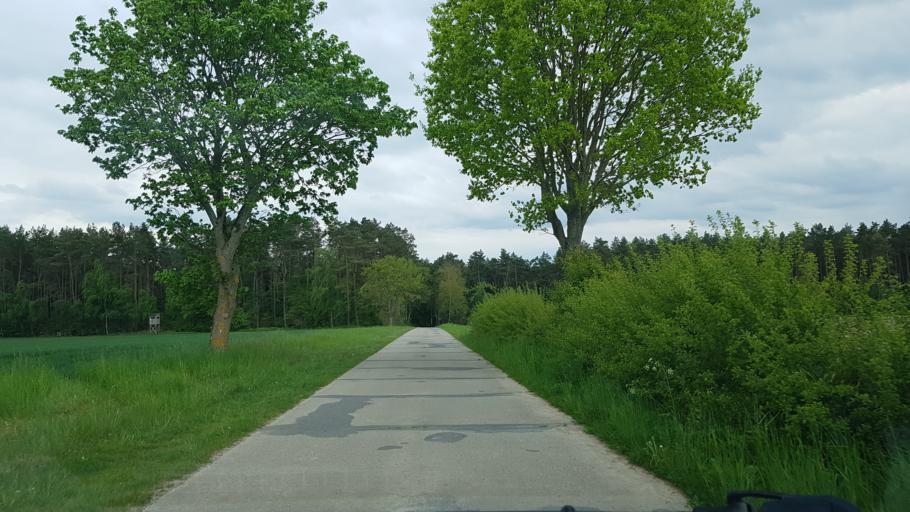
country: DE
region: Lower Saxony
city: Vastorf
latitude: 53.1771
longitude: 10.5509
